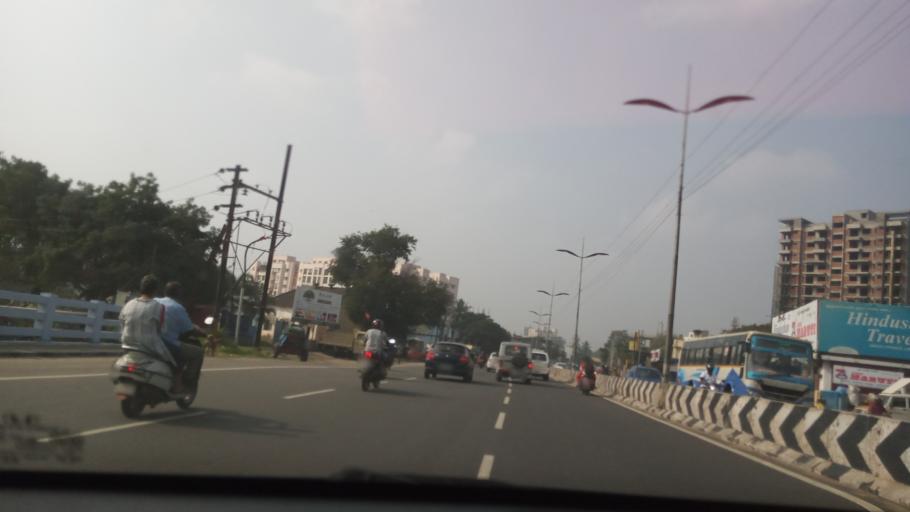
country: IN
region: Tamil Nadu
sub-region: Coimbatore
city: Coimbatore
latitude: 11.0173
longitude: 76.9903
